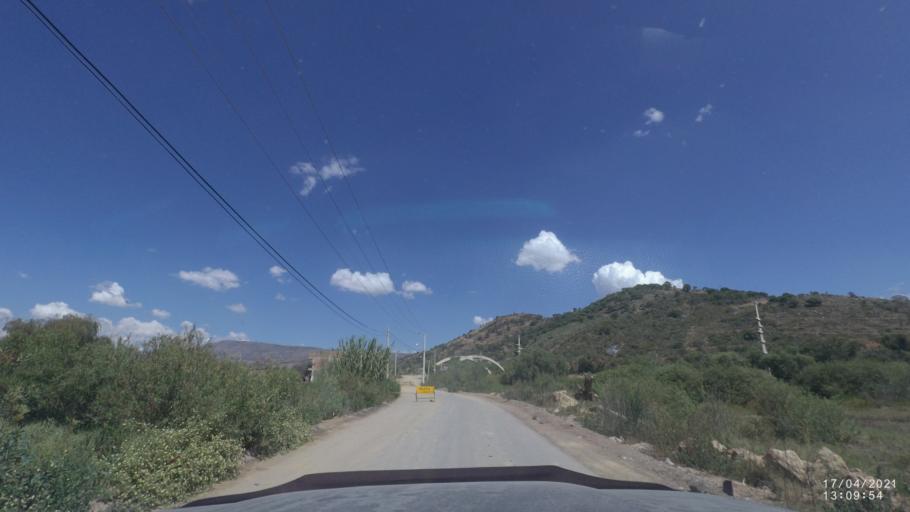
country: BO
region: Cochabamba
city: Cochabamba
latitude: -17.4162
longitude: -66.2241
